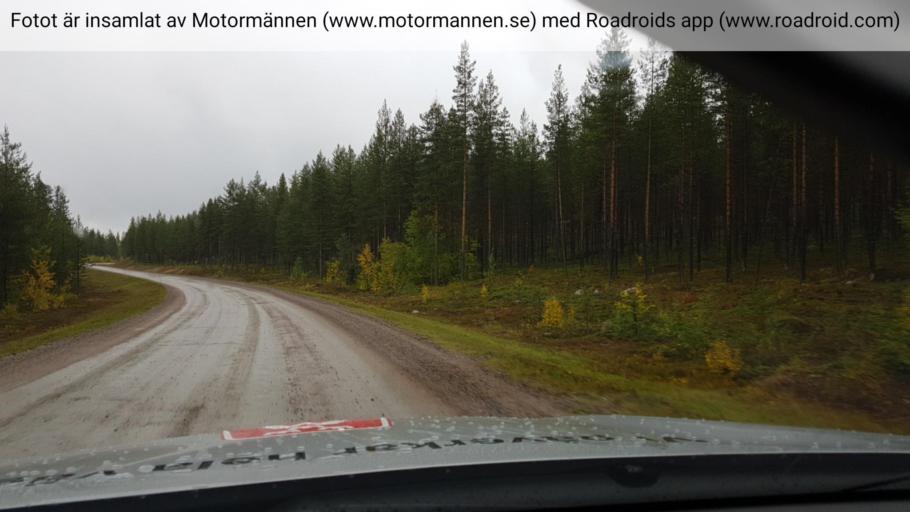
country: SE
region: Norrbotten
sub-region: Alvsbyns Kommun
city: AElvsbyn
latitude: 66.2710
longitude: 21.0893
